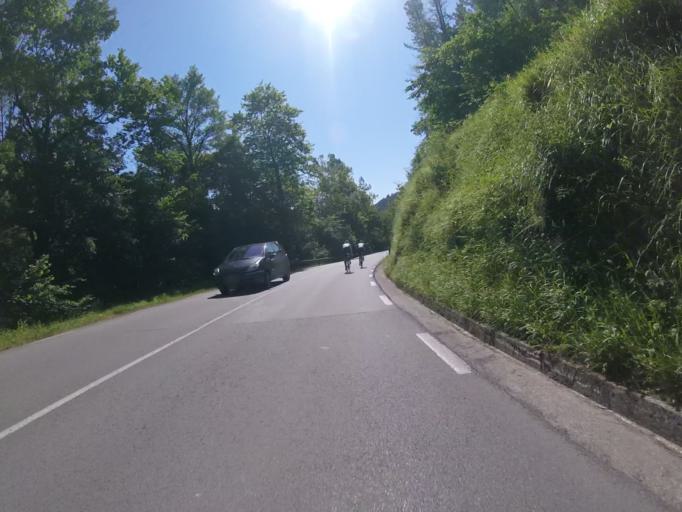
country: ES
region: Basque Country
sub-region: Provincia de Guipuzcoa
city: Albiztur
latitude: 43.1244
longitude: -2.1113
